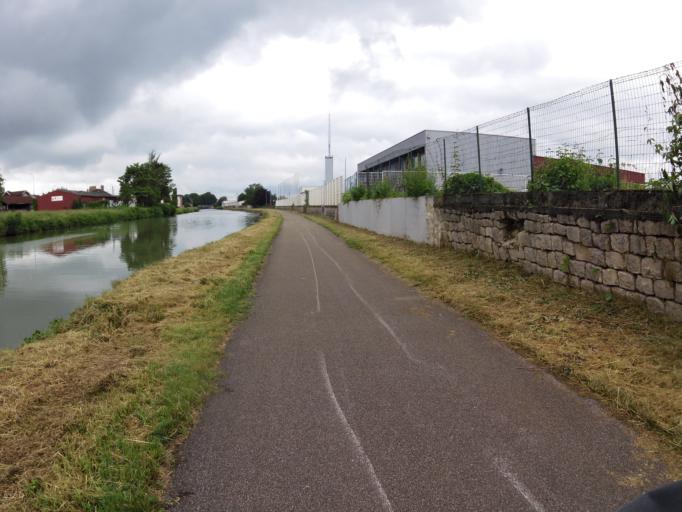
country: FR
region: Champagne-Ardenne
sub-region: Departement de la Haute-Marne
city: Saint-Dizier
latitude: 48.6422
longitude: 4.9446
